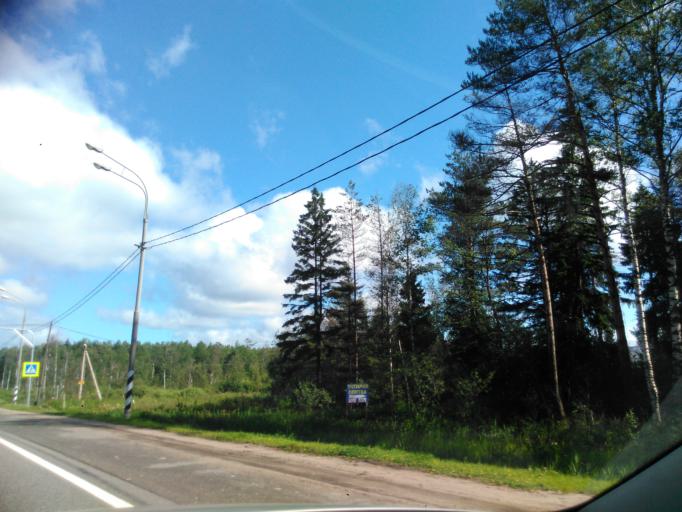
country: RU
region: Moskovskaya
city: Reshetnikovo
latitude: 56.4007
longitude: 36.6532
